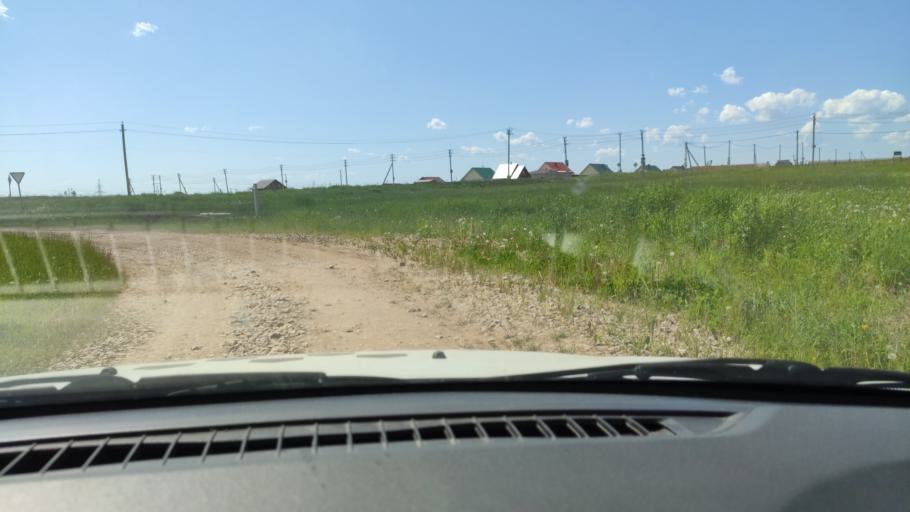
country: RU
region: Perm
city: Ferma
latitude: 57.9415
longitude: 56.3398
